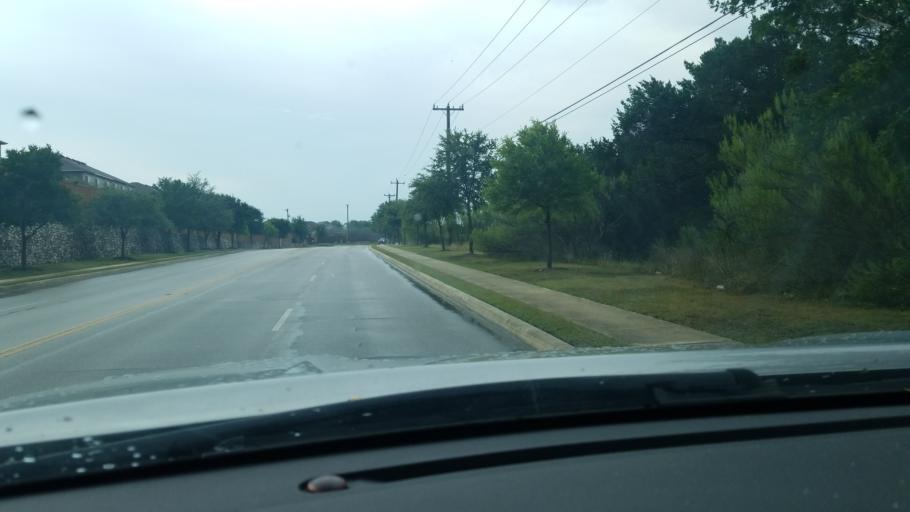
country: US
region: Texas
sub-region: Bexar County
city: Timberwood Park
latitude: 29.6982
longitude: -98.4814
